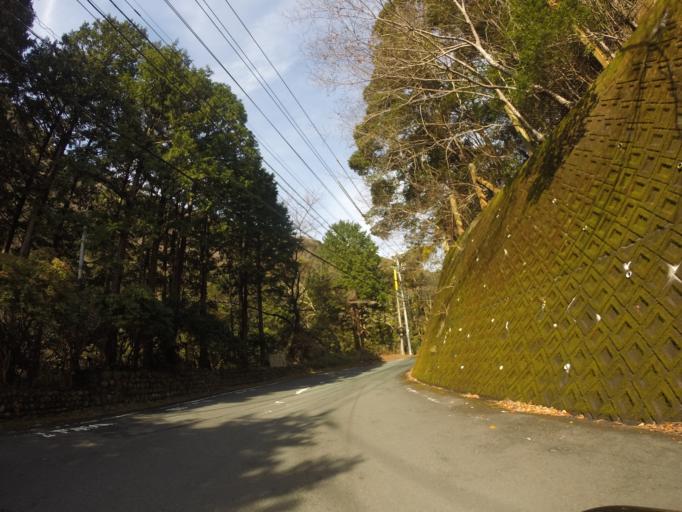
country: JP
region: Shizuoka
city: Heda
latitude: 34.8098
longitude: 138.8226
